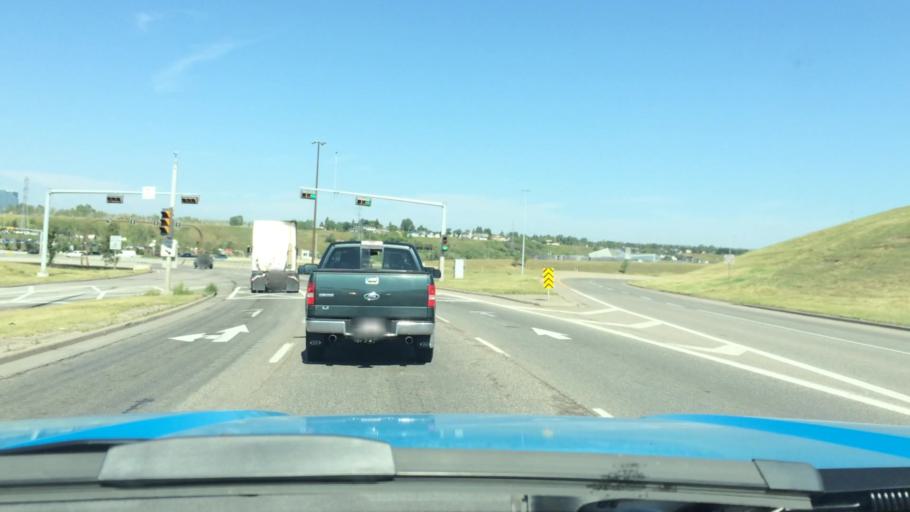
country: CA
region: Alberta
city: Calgary
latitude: 51.0489
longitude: -114.0156
